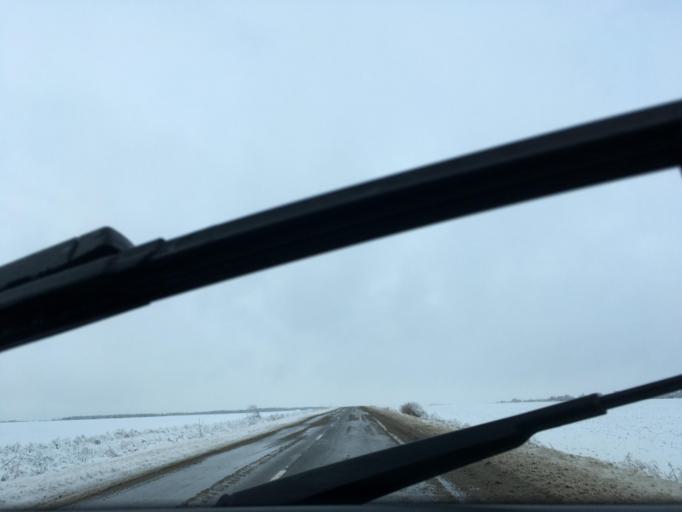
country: RU
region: Voronezj
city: Ol'khovatka
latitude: 50.1385
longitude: 39.2045
